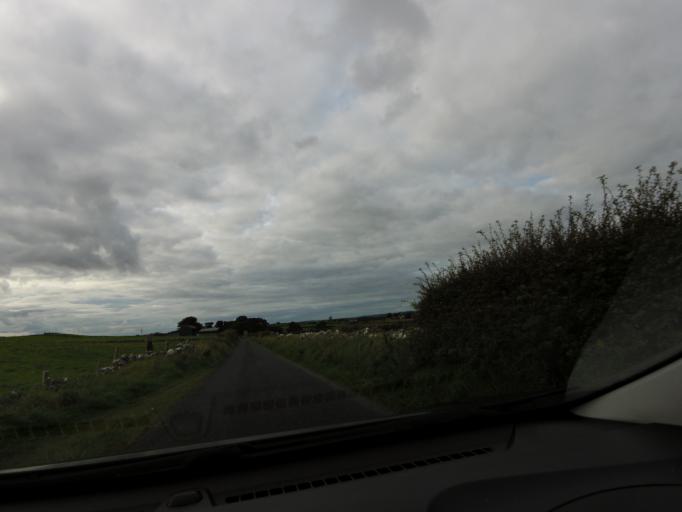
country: IE
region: Connaught
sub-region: County Galway
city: Ballinasloe
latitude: 53.3717
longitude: -8.1650
